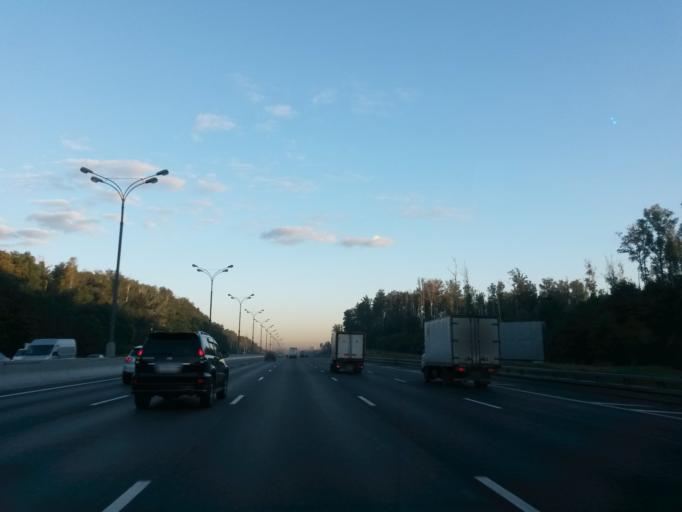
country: RU
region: Moskovskaya
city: Druzhba
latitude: 55.8573
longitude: 37.7751
